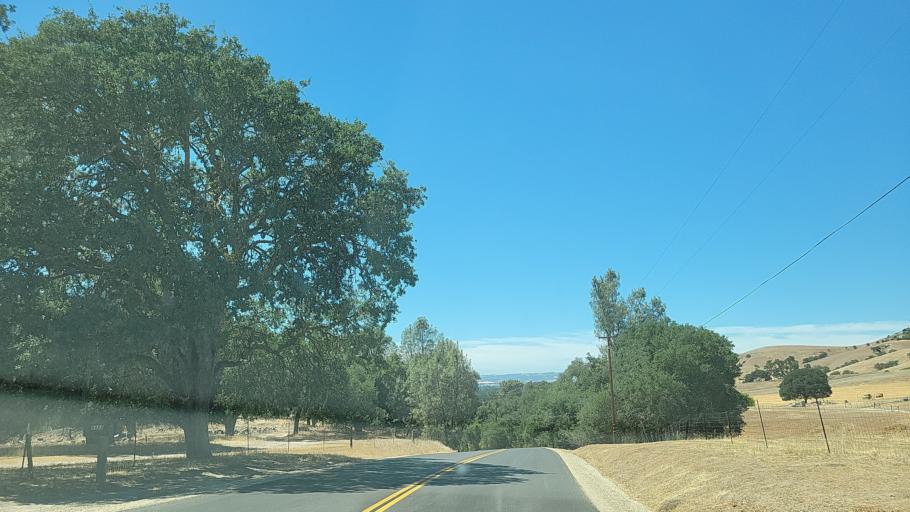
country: US
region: California
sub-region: San Luis Obispo County
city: Atascadero
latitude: 35.4793
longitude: -120.6252
